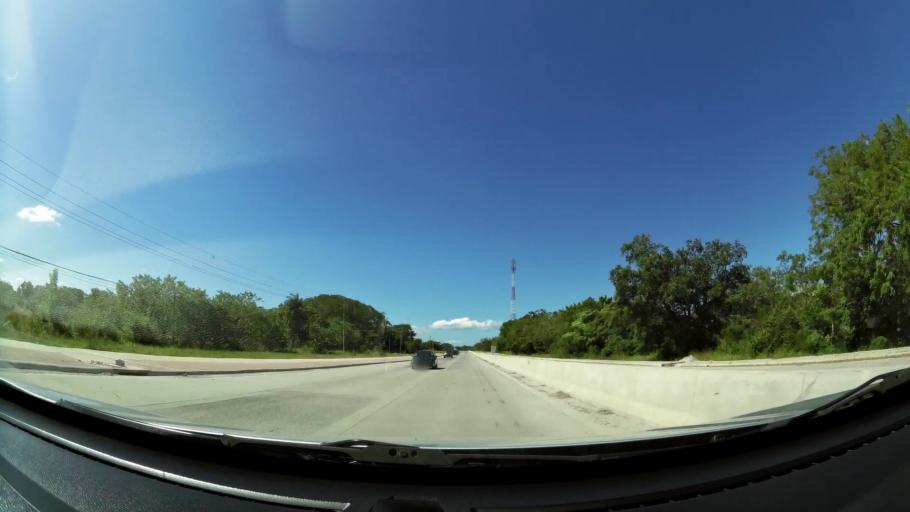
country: CR
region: Guanacaste
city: Liberia
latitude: 10.5544
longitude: -85.3722
